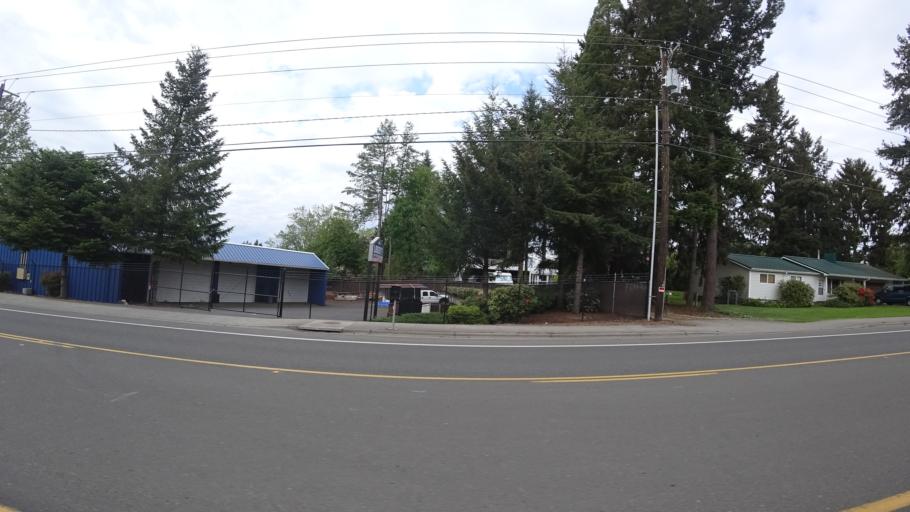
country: US
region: Oregon
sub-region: Washington County
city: Hillsboro
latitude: 45.4973
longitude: -122.9467
